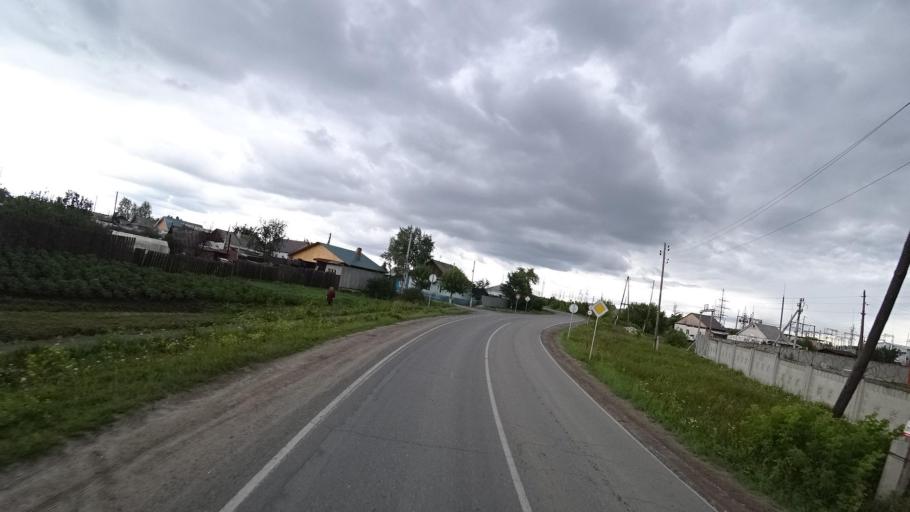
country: RU
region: Sverdlovsk
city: Kamyshlov
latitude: 56.8494
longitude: 62.7425
